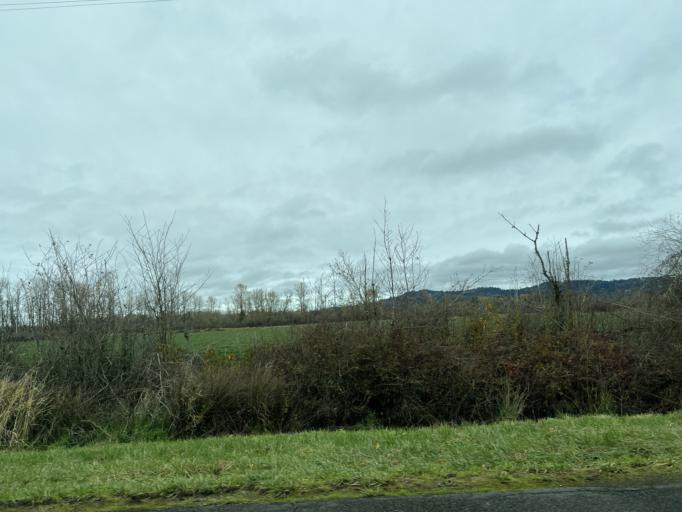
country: US
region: Oregon
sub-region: Marion County
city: Jefferson
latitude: 44.7950
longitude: -123.0867
